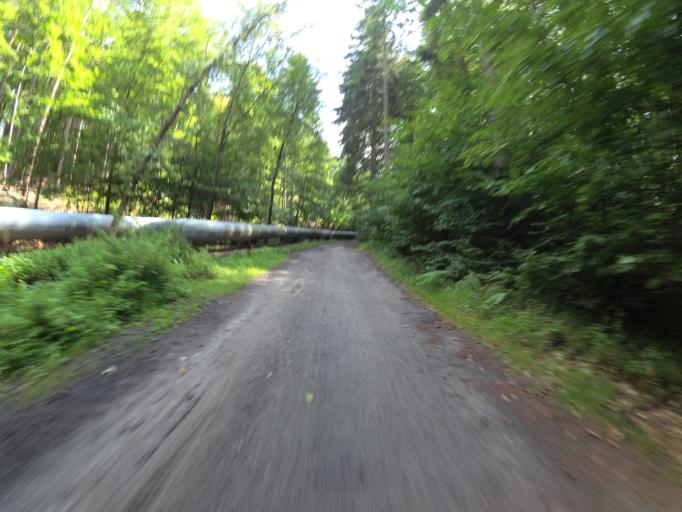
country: PL
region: Pomeranian Voivodeship
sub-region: Gdynia
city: Wielki Kack
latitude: 54.5098
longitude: 18.4871
